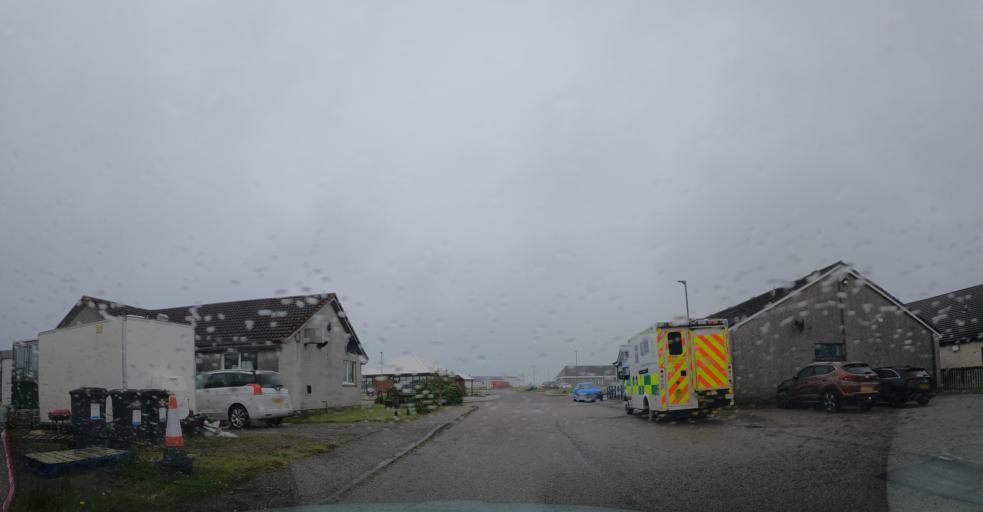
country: GB
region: Scotland
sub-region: Eilean Siar
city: Benbecula
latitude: 57.4723
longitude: -7.3786
